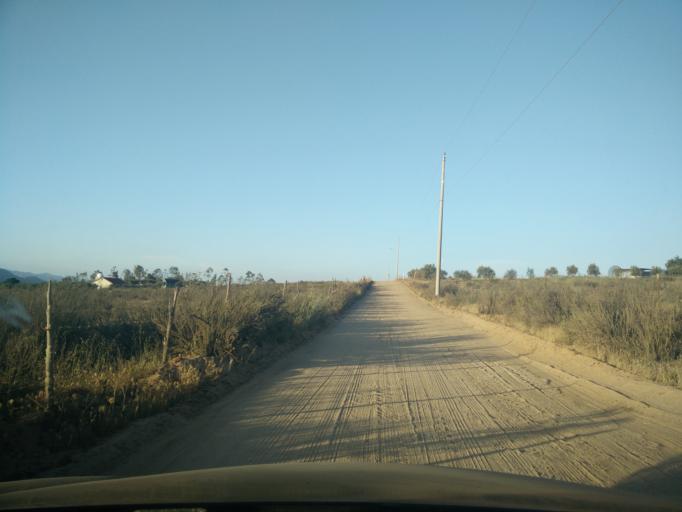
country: MX
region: Baja California
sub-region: Ensenada
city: Rancho Verde
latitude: 32.0433
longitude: -116.6525
